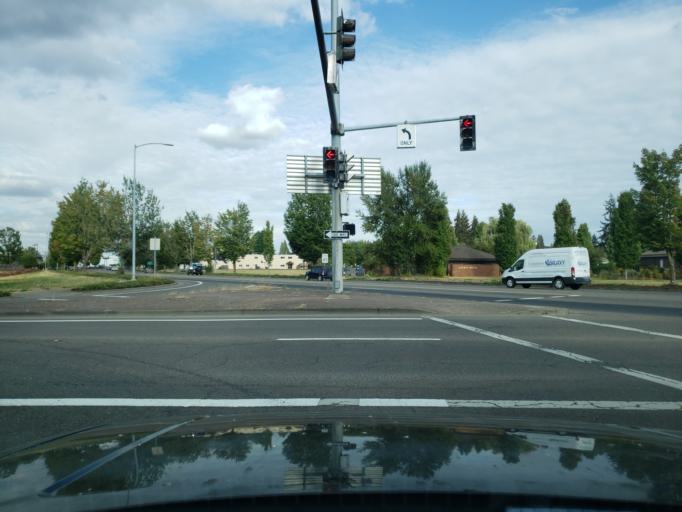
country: US
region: Oregon
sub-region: Marion County
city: Salem
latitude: 44.9664
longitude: -123.0320
